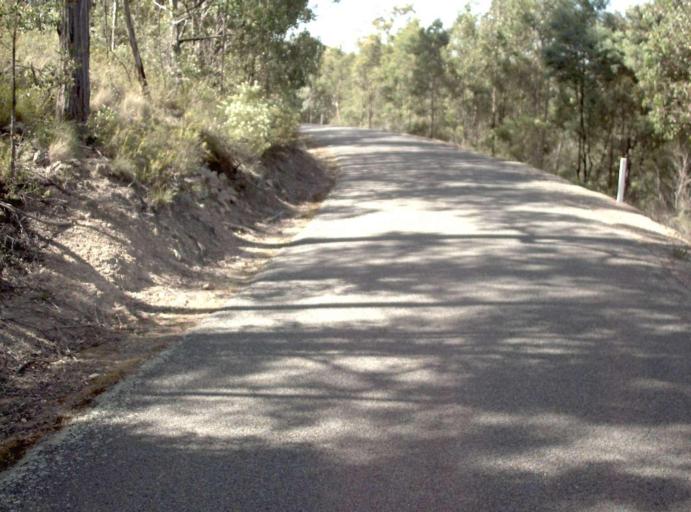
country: AU
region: Victoria
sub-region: East Gippsland
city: Lakes Entrance
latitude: -37.4860
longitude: 148.1279
